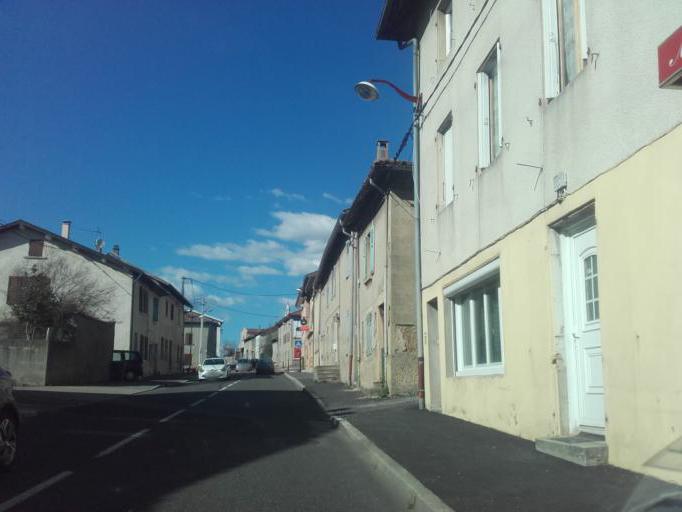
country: FR
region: Rhone-Alpes
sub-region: Departement de l'Isere
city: Champier
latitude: 45.5012
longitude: 5.3020
